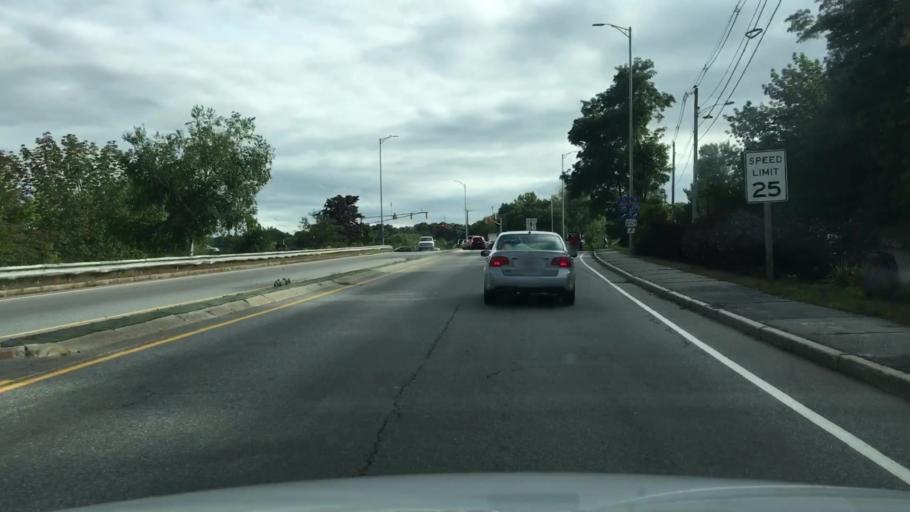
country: US
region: Maine
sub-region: Kennebec County
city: Gardiner
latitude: 44.2349
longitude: -69.7721
